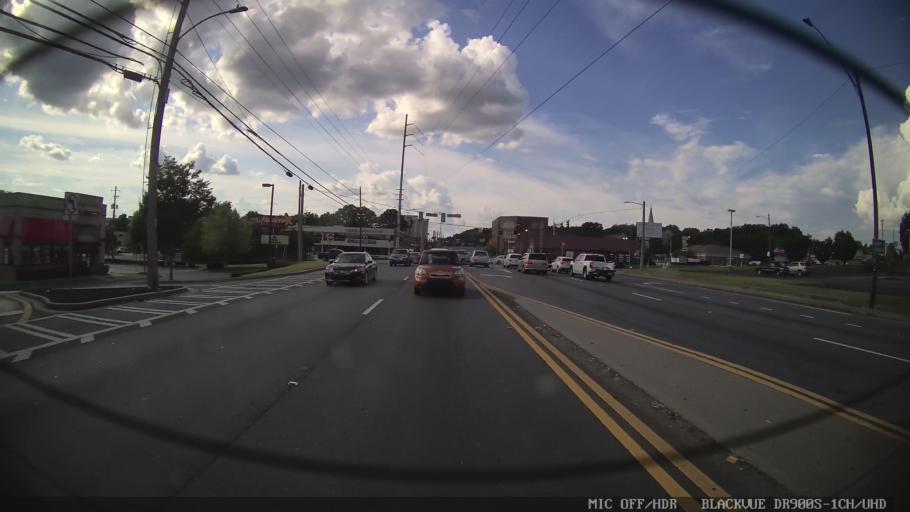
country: US
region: Georgia
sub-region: Floyd County
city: Rome
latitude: 34.2558
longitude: -85.1644
